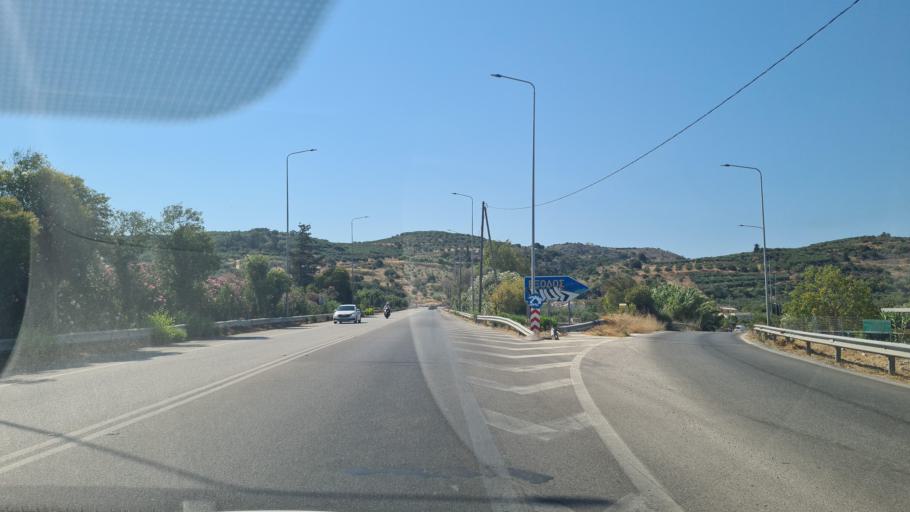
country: GR
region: Crete
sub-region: Nomos Chanias
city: Kalivai
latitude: 35.4446
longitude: 24.1691
